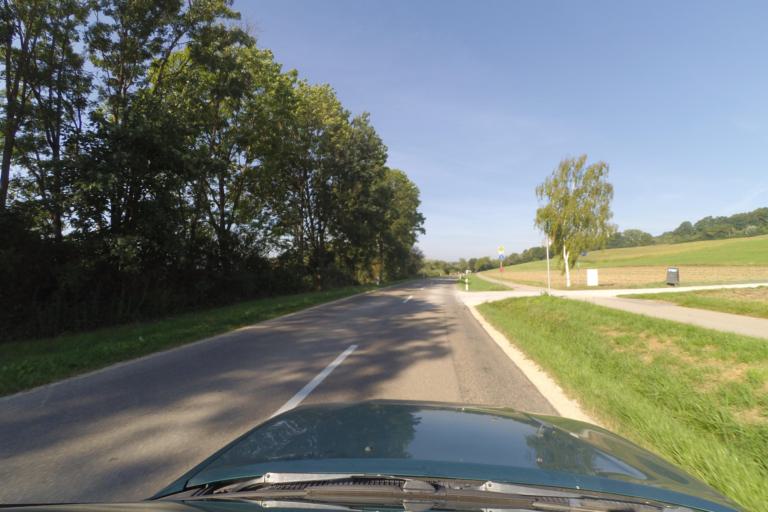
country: DE
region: Bavaria
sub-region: Swabia
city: Asbach-Baumenheim
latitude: 48.7161
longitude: 10.8383
